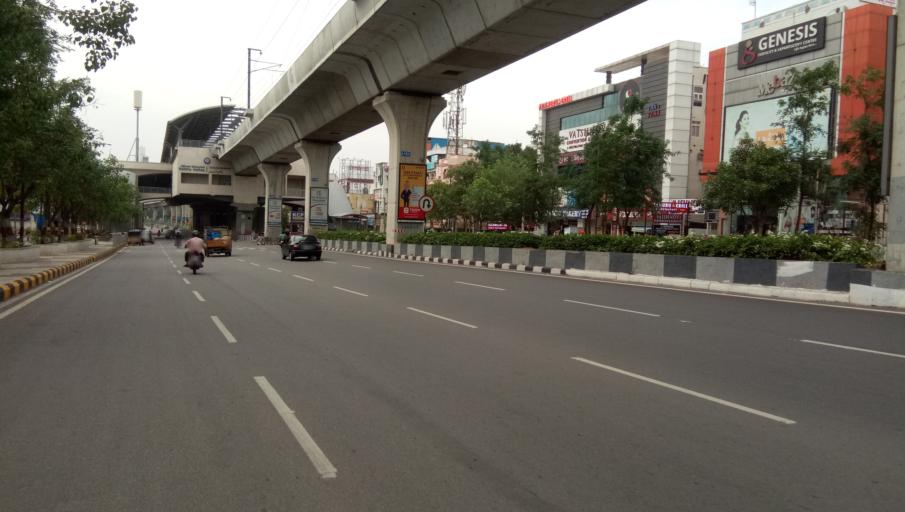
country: IN
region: Telangana
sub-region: Rangareddi
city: Lal Bahadur Nagar
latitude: 17.3601
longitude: 78.5443
